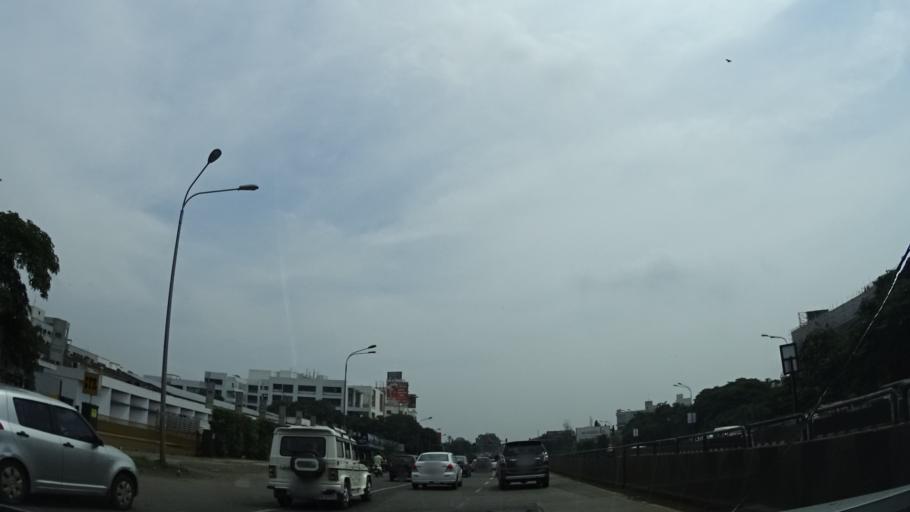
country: IN
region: Maharashtra
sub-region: Pune Division
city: Lohogaon
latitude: 18.5614
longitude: 73.9199
